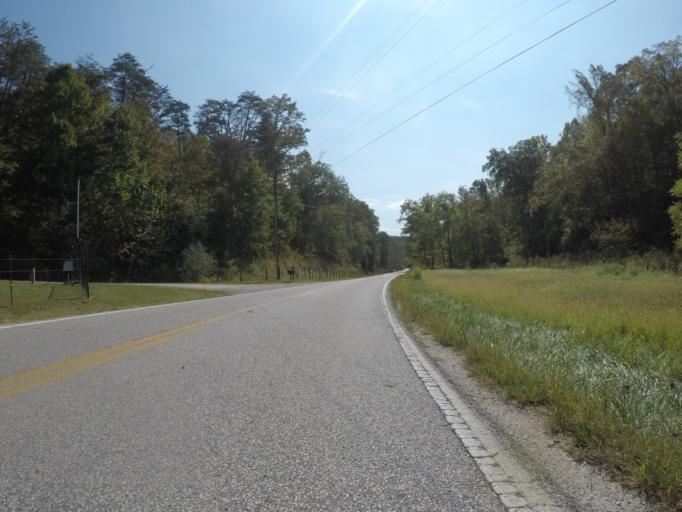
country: US
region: West Virginia
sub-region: Cabell County
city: Lesage
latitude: 38.5785
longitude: -82.4106
